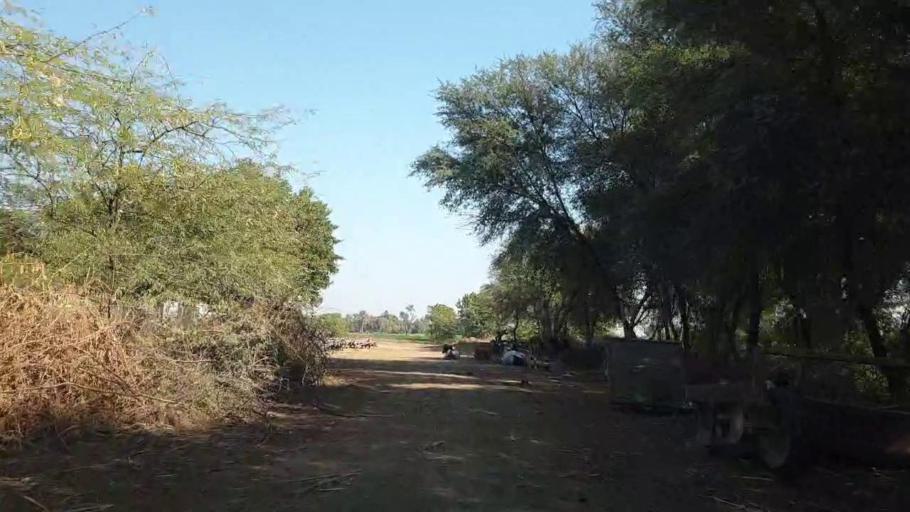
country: PK
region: Sindh
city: Tando Adam
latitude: 25.6452
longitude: 68.6857
